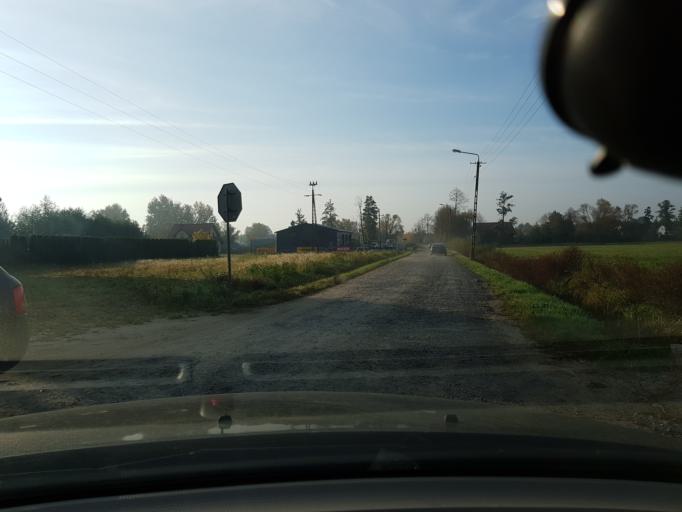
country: PL
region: Masovian Voivodeship
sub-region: Powiat minski
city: Halinow
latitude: 52.1893
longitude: 21.3128
